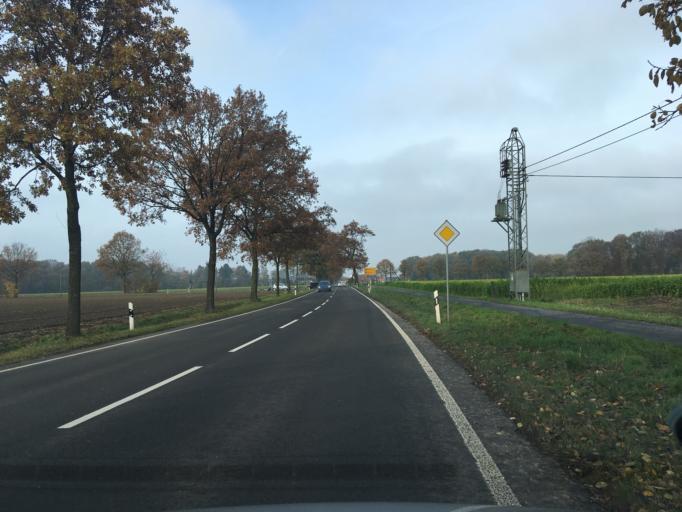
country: DE
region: North Rhine-Westphalia
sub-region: Regierungsbezirk Munster
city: Sudlohn
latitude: 51.9292
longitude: 6.8829
